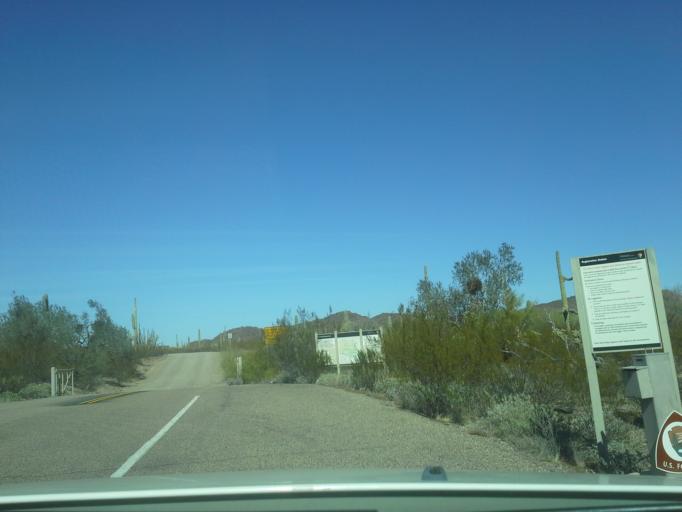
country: MX
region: Sonora
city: Sonoyta
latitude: 31.9558
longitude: -112.8036
